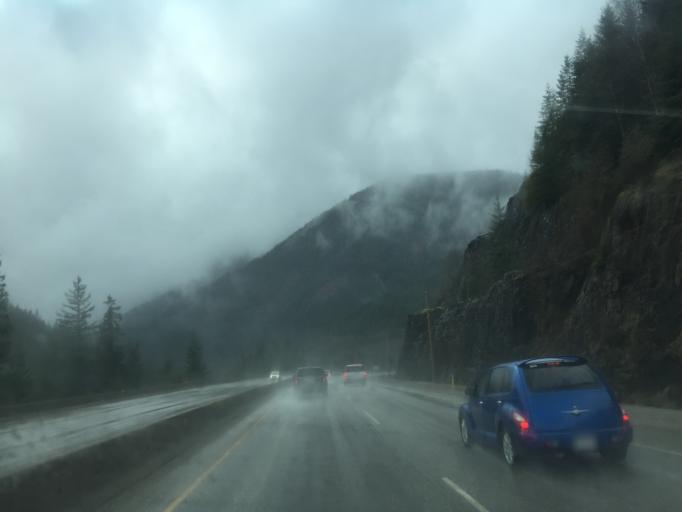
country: CA
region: British Columbia
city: Hope
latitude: 49.4949
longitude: -121.2319
